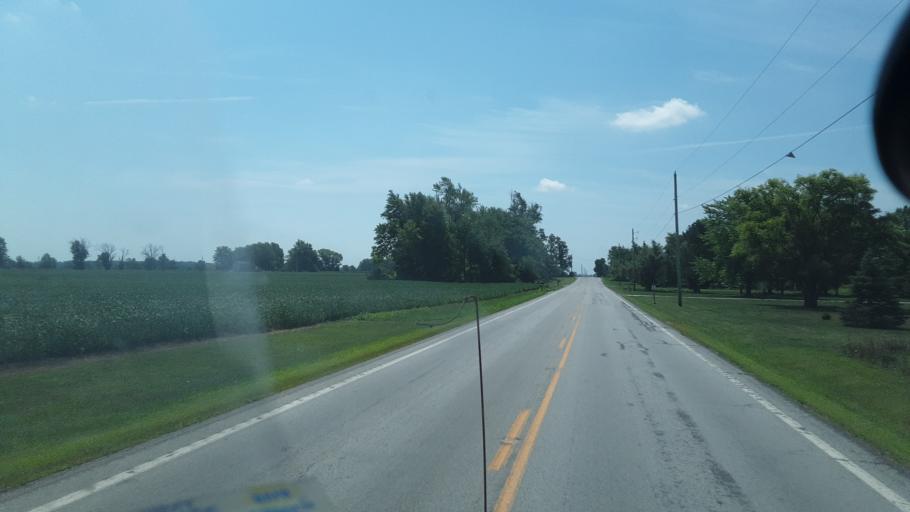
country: US
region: Ohio
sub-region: Hancock County
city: Arlington
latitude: 40.9611
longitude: -83.5747
